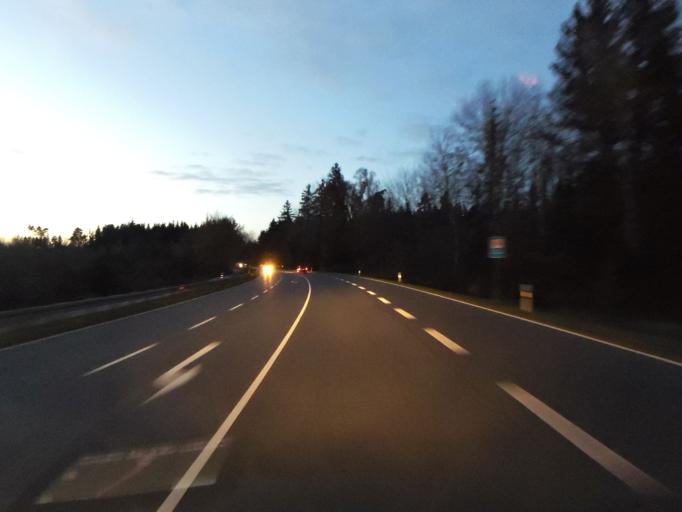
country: DE
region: Bavaria
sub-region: Upper Bavaria
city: Hohenbrunn
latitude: 48.0277
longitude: 11.6954
